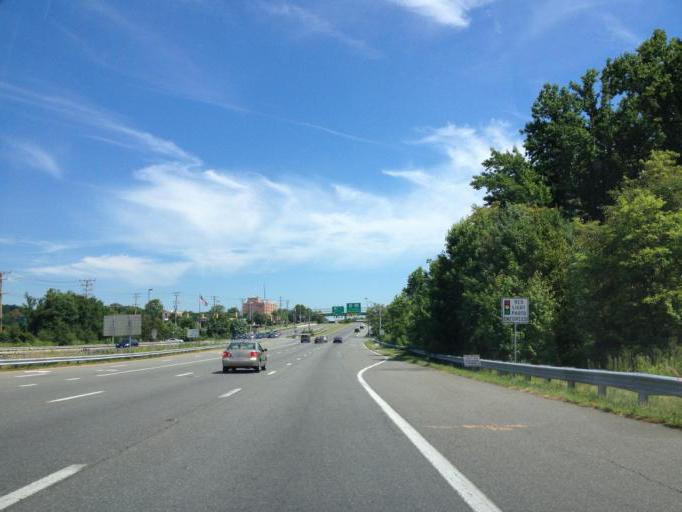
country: US
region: Maryland
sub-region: Prince George's County
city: Bowie
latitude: 38.9469
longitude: -76.7178
